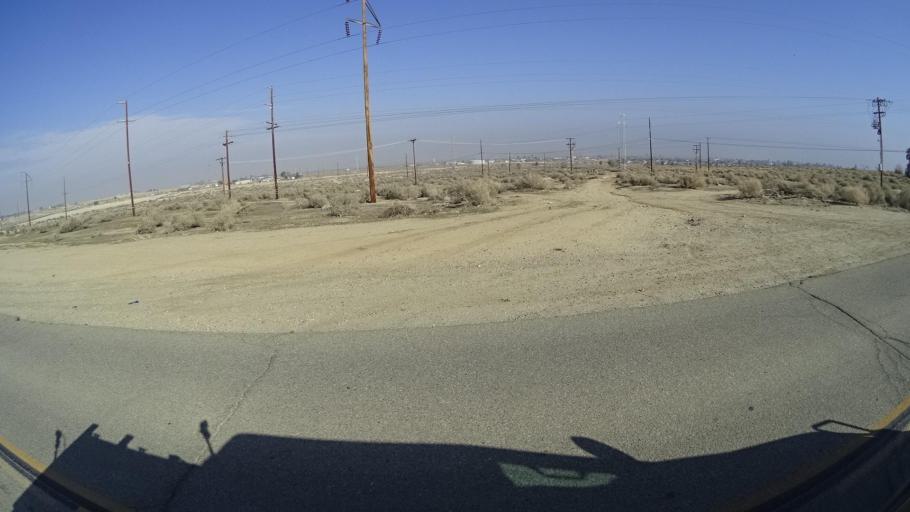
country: US
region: California
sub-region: Kern County
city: Taft Heights
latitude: 35.1381
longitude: -119.4843
